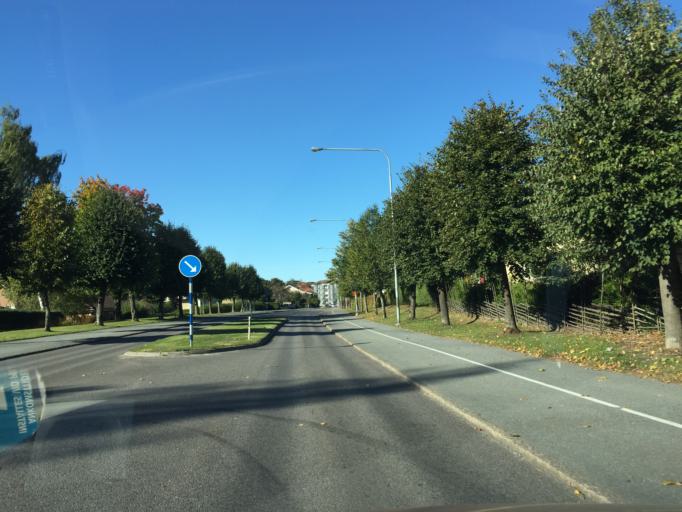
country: SE
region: OErebro
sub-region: Kumla Kommun
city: Kumla
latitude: 59.1239
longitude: 15.1501
